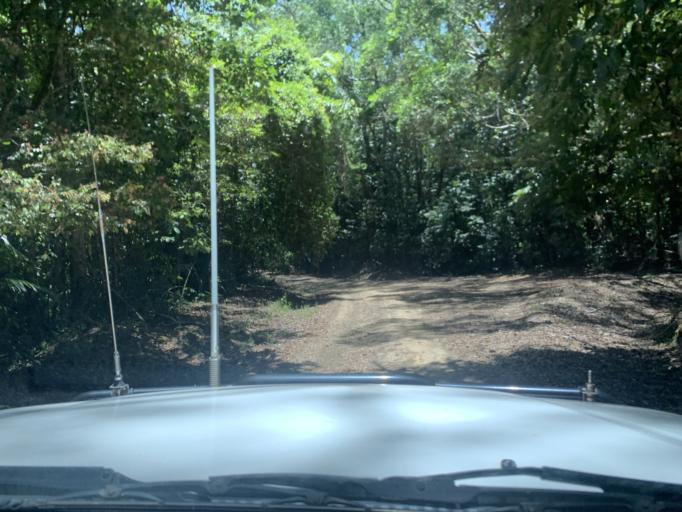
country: AU
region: Queensland
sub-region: Cairns
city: Redlynch
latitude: -16.9449
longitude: 145.6329
